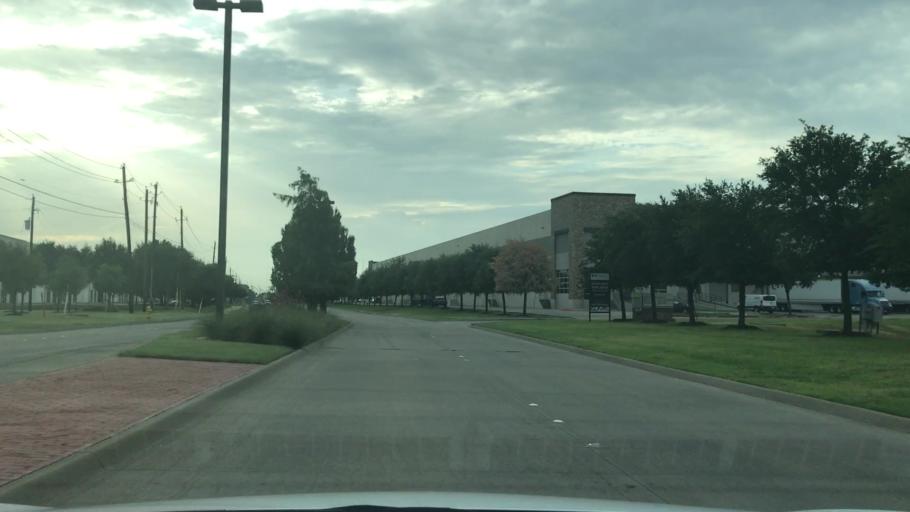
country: US
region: Texas
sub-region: Dallas County
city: Coppell
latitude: 32.9548
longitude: -97.0162
